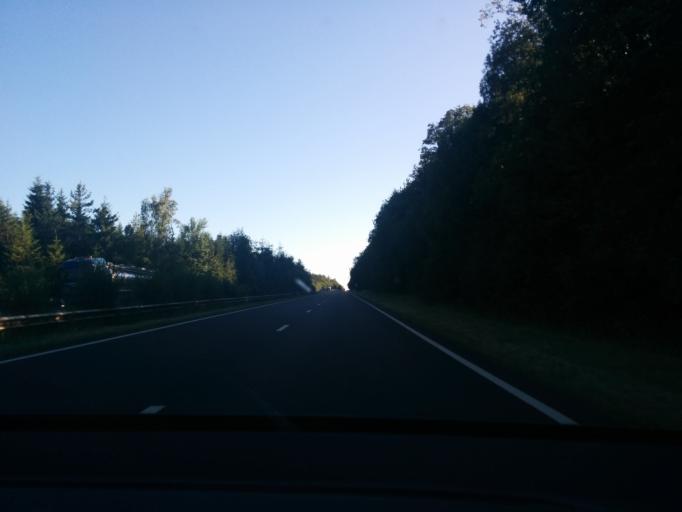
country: BE
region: Wallonia
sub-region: Province du Luxembourg
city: Saint-Hubert
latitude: 50.0670
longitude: 5.4198
